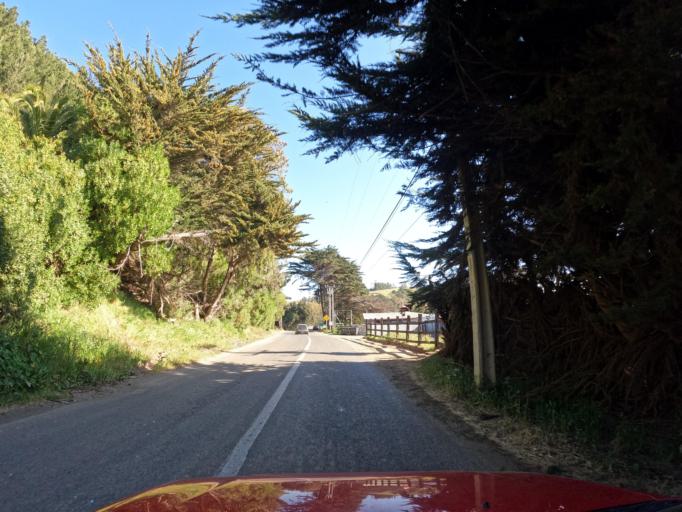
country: CL
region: Maule
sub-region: Provincia de Talca
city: Constitucion
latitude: -34.8787
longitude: -72.1555
